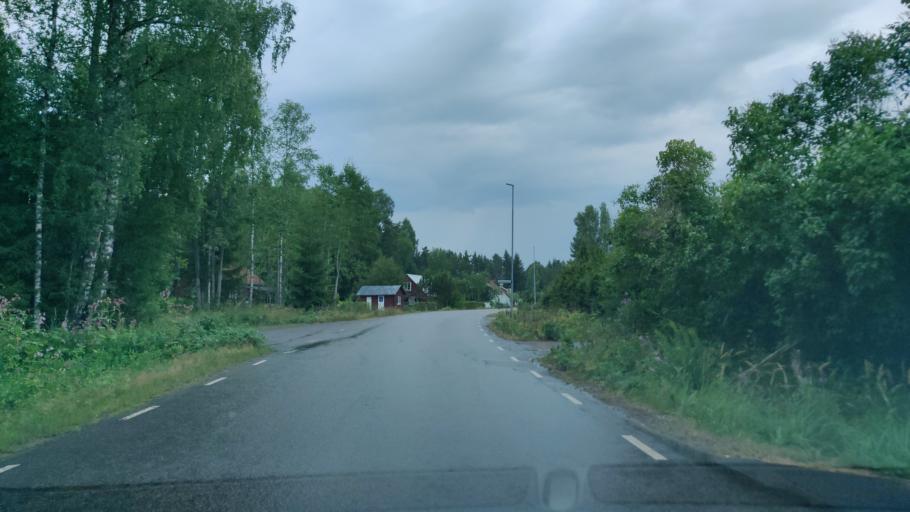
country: SE
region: Vaermland
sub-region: Munkfors Kommun
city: Munkfors
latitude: 59.8594
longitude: 13.5510
